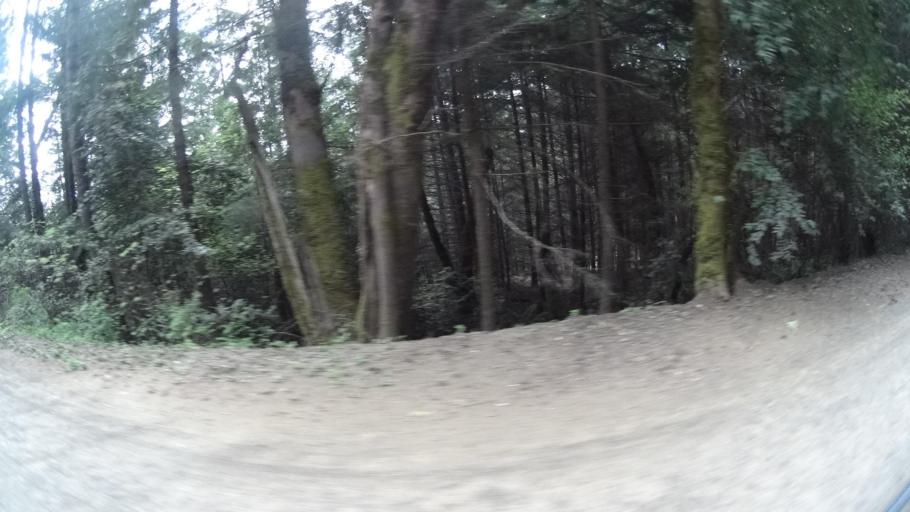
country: US
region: California
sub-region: Humboldt County
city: Redway
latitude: 40.2468
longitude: -123.7656
